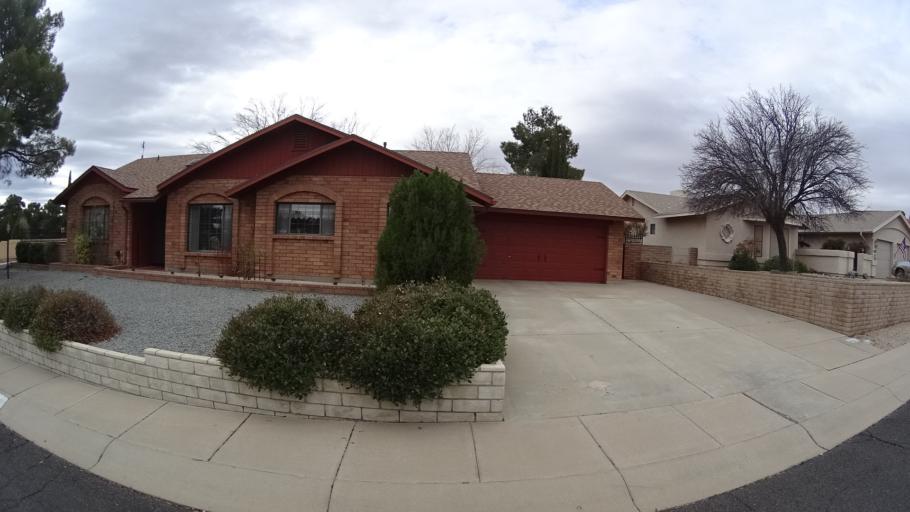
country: US
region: Arizona
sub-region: Mohave County
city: New Kingman-Butler
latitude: 35.2371
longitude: -114.0461
